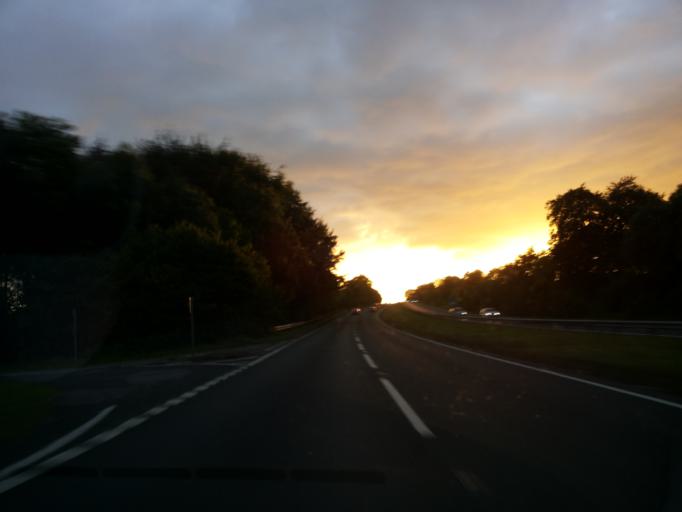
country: GB
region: England
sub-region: Hampshire
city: Abbotts Ann
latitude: 51.2063
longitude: -1.5872
